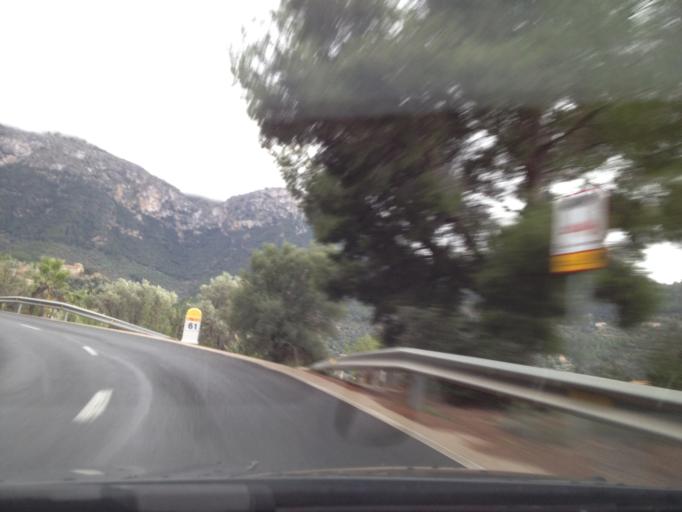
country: ES
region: Balearic Islands
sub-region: Illes Balears
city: Deia
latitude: 39.7566
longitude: 2.6468
